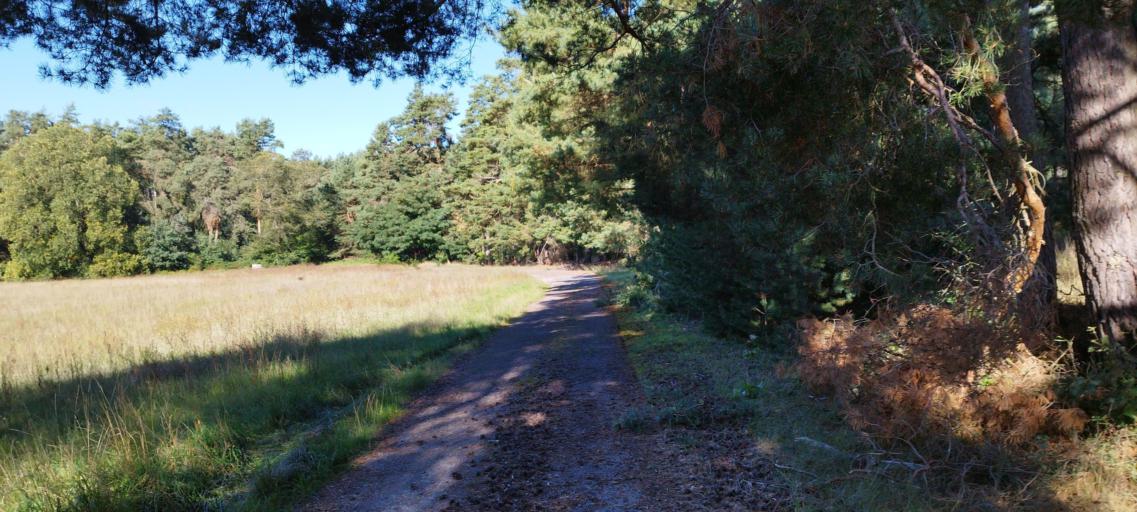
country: DE
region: Brandenburg
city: Lawitz
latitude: 52.1066
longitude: 14.5654
